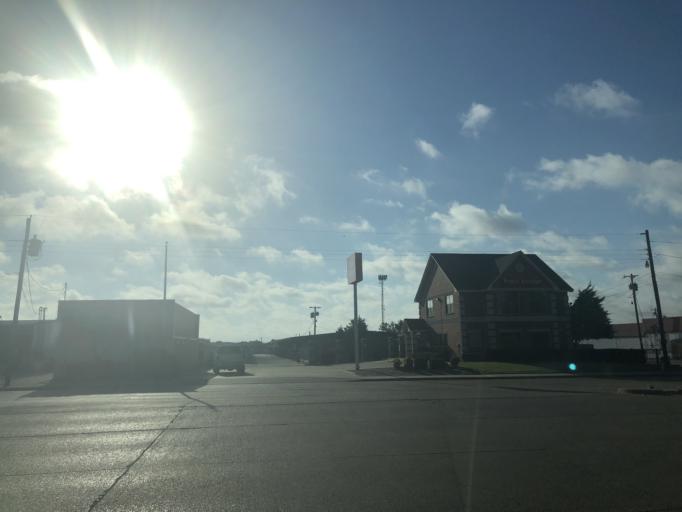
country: US
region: Texas
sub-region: Dallas County
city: Duncanville
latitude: 32.6702
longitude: -96.9088
